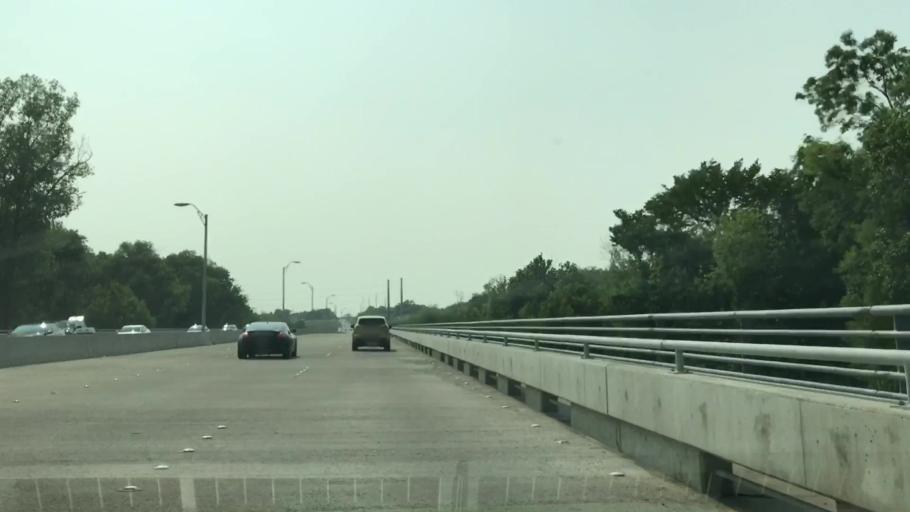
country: US
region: Texas
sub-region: Dallas County
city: Rowlett
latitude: 32.8940
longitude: -96.5893
